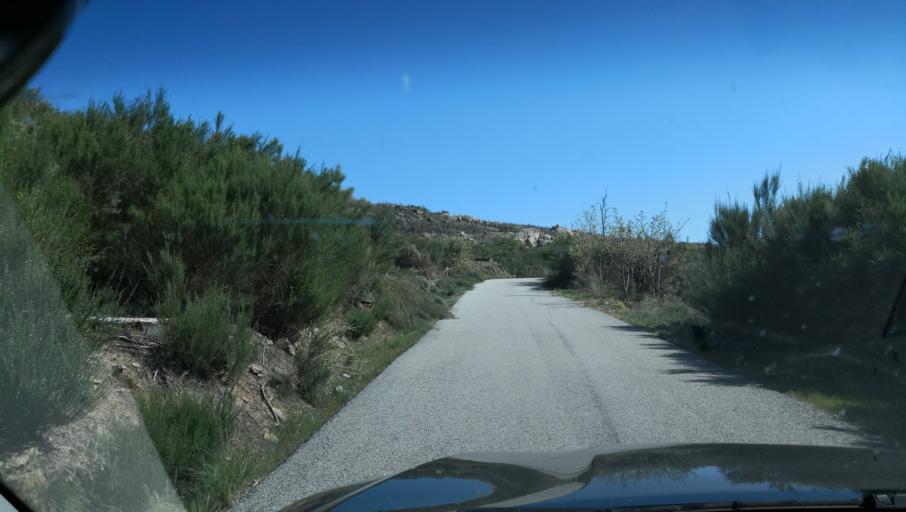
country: PT
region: Vila Real
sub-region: Sabrosa
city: Sabrosa
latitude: 41.2960
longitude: -7.6378
